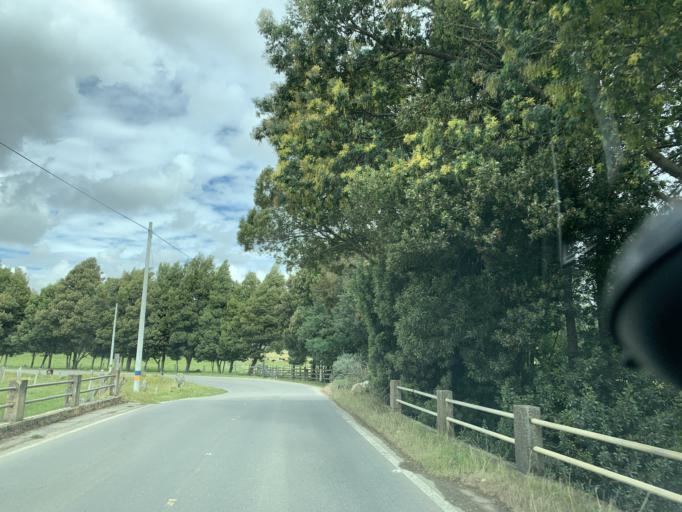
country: CO
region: Boyaca
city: Toca
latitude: 5.5746
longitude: -73.2163
